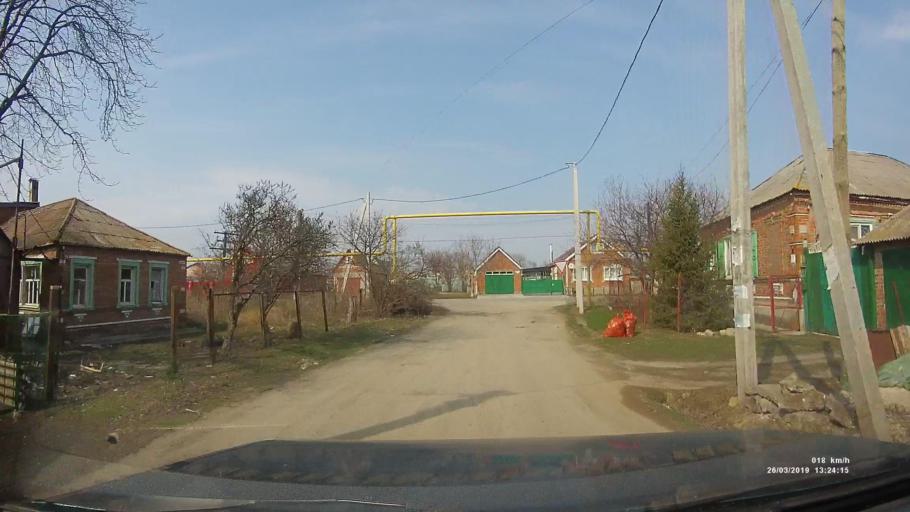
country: RU
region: Rostov
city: Novobessergenovka
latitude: 47.1745
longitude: 38.7659
